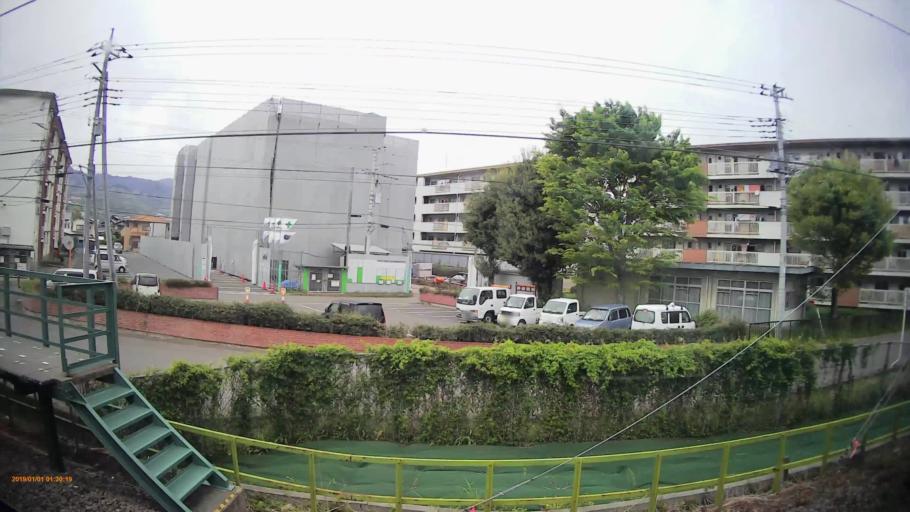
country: JP
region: Yamanashi
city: Enzan
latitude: 35.6948
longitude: 138.7038
